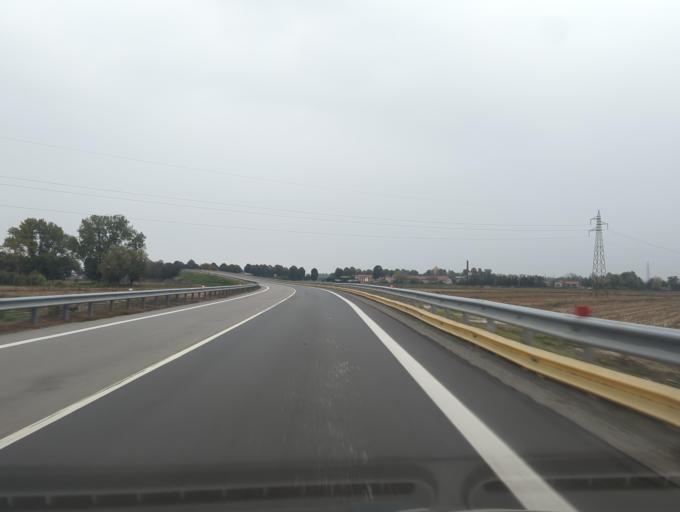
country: IT
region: Piedmont
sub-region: Provincia di Novara
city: Romentino
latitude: 45.4731
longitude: 8.7141
